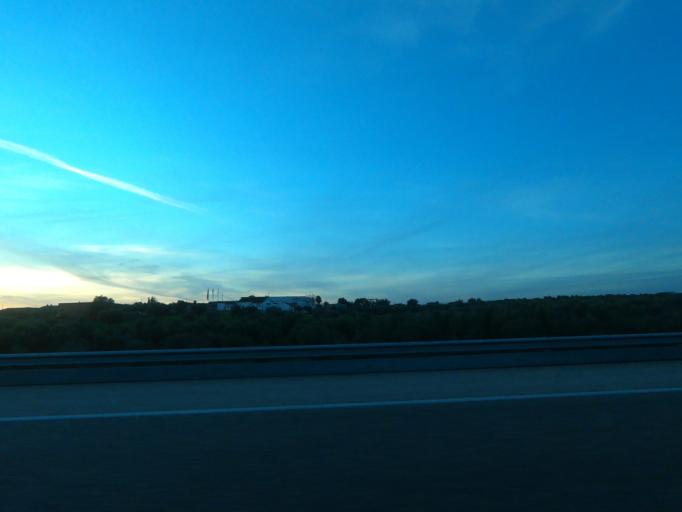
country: PT
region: Santarem
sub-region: Alcanena
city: Alcanena
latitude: 39.4192
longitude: -8.6326
